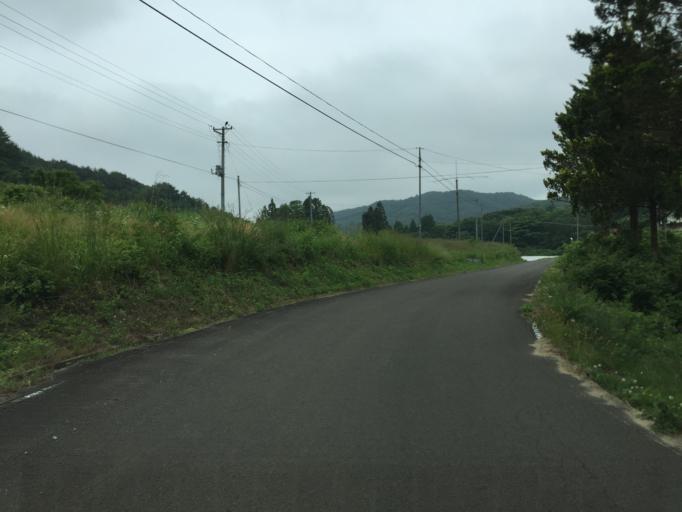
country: JP
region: Fukushima
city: Yanagawamachi-saiwaicho
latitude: 37.7810
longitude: 140.7048
